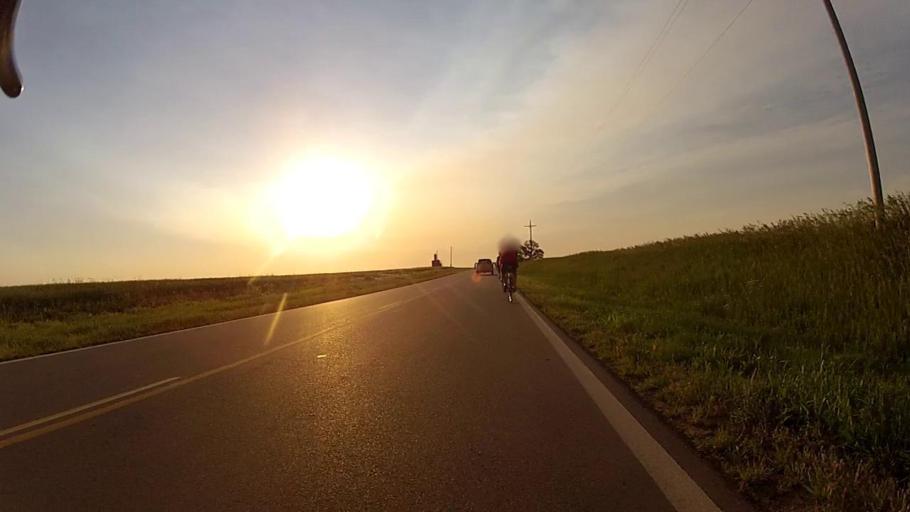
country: US
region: Kansas
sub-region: Harper County
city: Anthony
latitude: 37.1527
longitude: -97.9465
